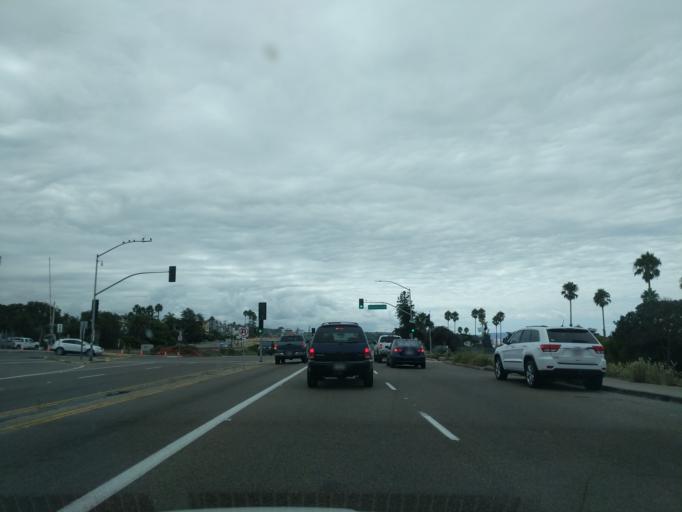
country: US
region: California
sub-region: San Diego County
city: Encinitas
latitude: 33.0195
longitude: -117.2826
